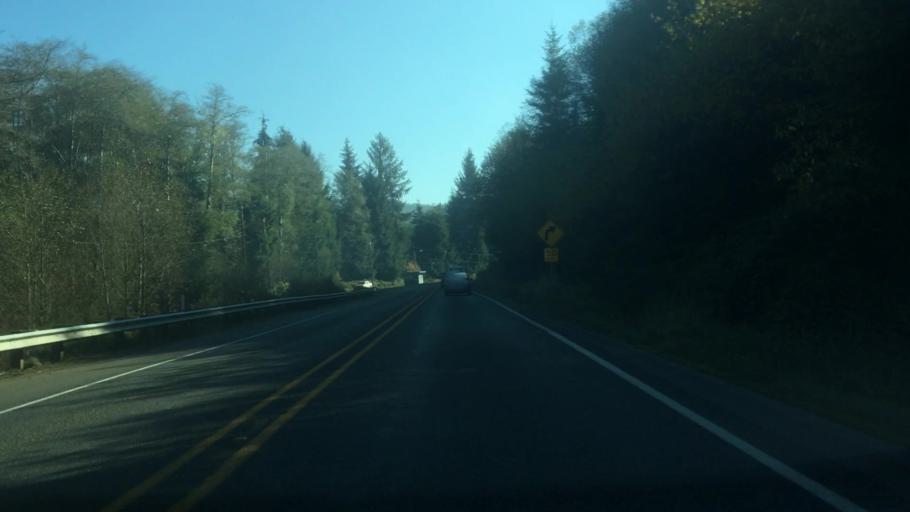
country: US
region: Washington
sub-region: Grays Harbor County
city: Central Park
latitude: 46.9161
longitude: -123.7180
